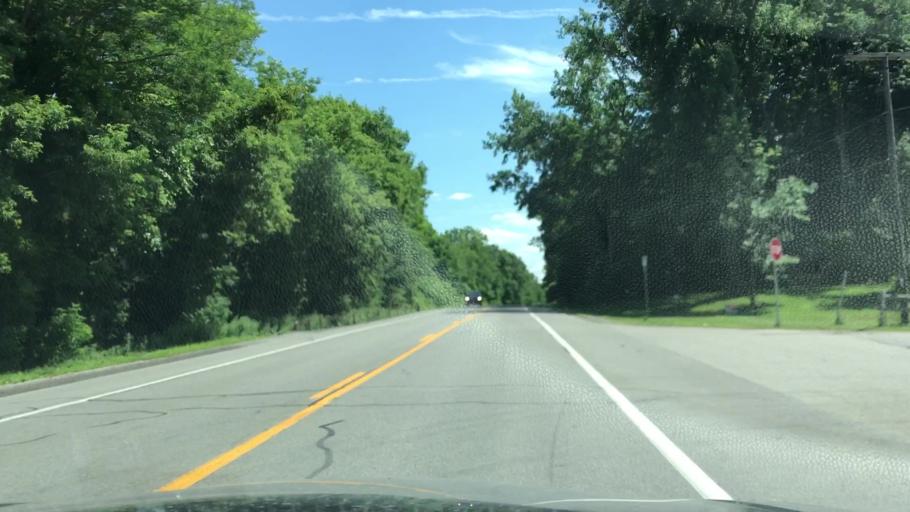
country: US
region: New York
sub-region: Livingston County
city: Mount Morris
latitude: 42.7529
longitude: -77.8838
